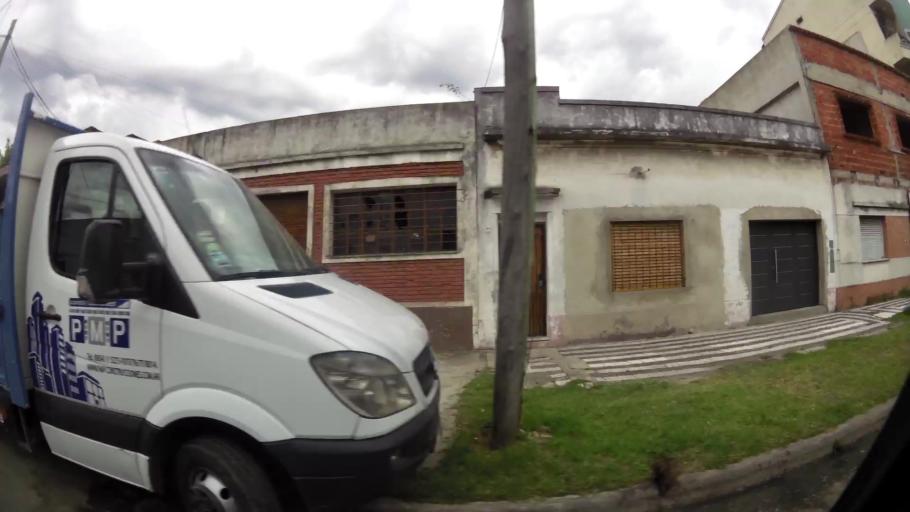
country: AR
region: Buenos Aires
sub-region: Partido de Lanus
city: Lanus
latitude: -34.6926
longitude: -58.3968
